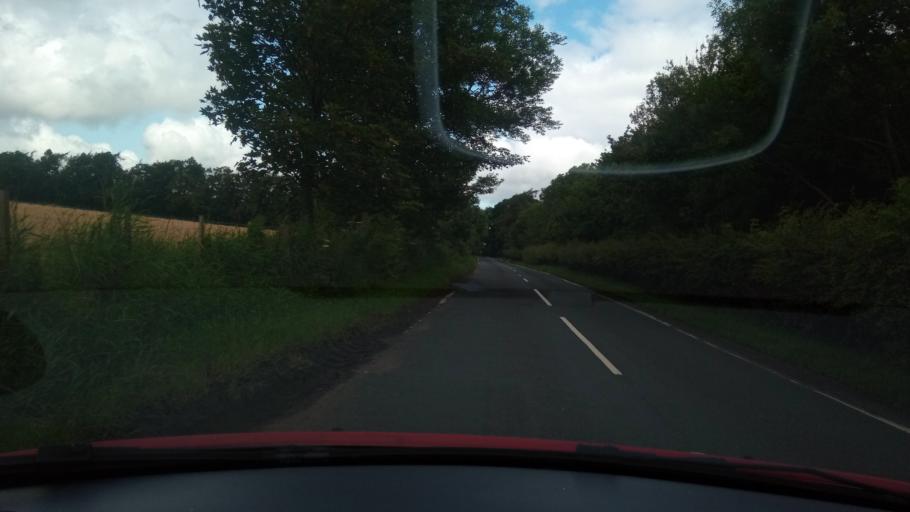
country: GB
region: Scotland
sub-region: East Lothian
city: Pencaitland
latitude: 55.8410
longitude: -2.8664
